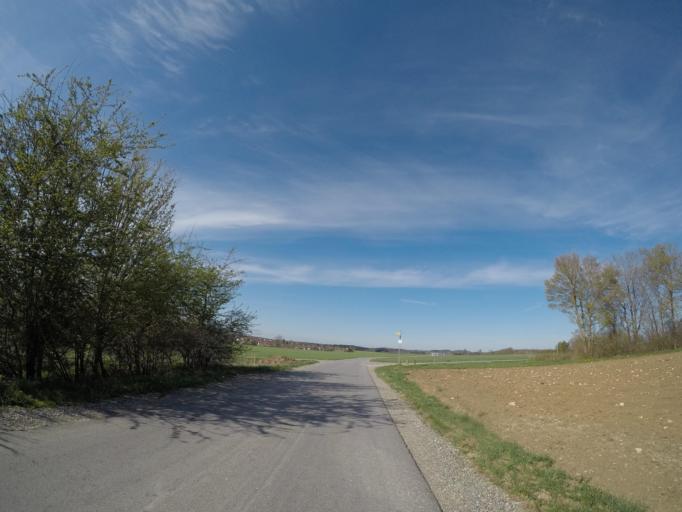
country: DE
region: Baden-Wuerttemberg
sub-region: Tuebingen Region
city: Allmendingen
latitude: 48.3509
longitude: 9.6525
